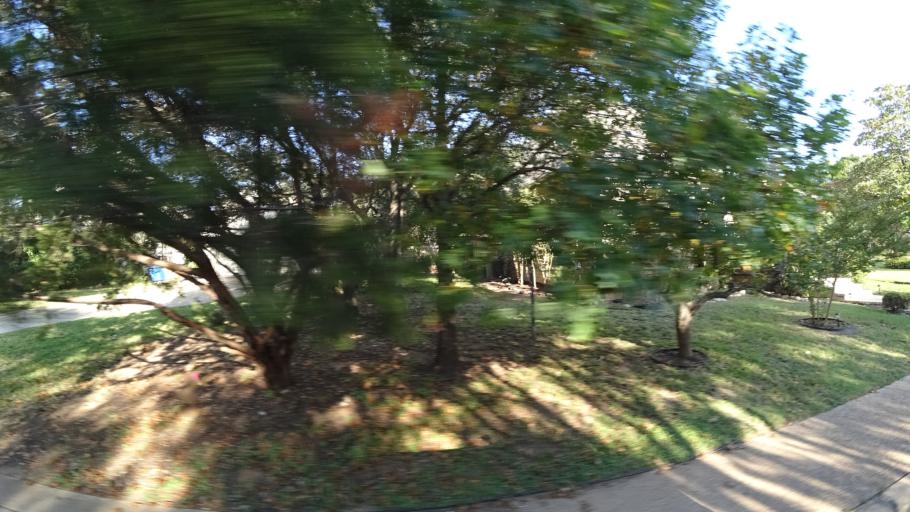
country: US
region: Texas
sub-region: Williamson County
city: Anderson Mill
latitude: 30.4303
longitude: -97.8133
